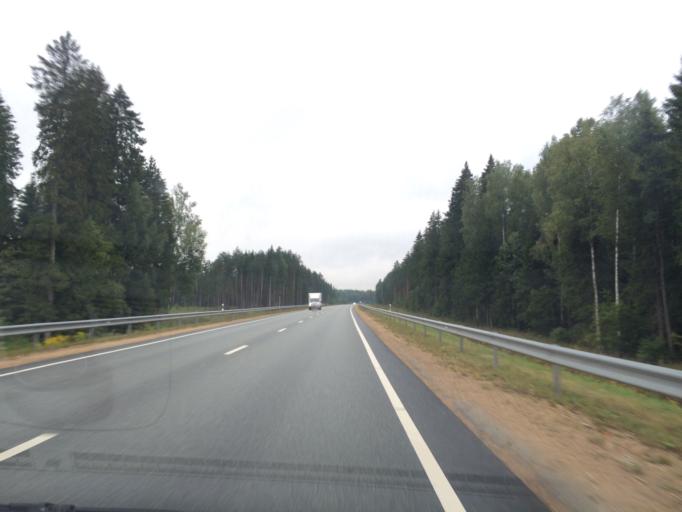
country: LV
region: Ogre
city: Ogre
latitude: 56.8521
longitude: 24.6548
